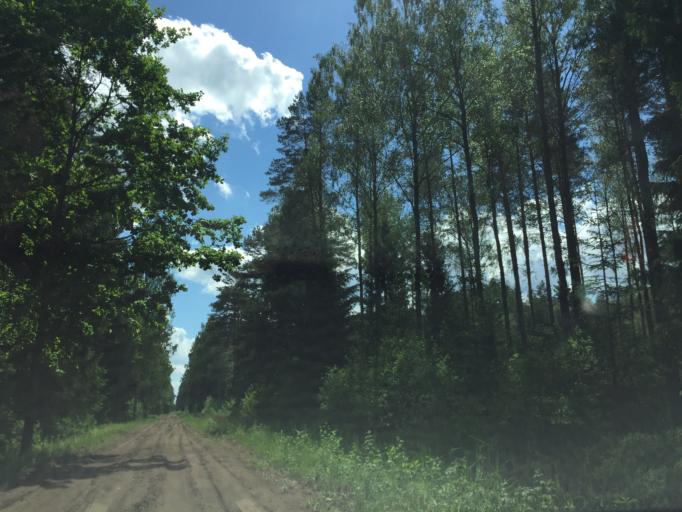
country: LV
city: Tireli
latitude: 56.8492
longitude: 23.6834
